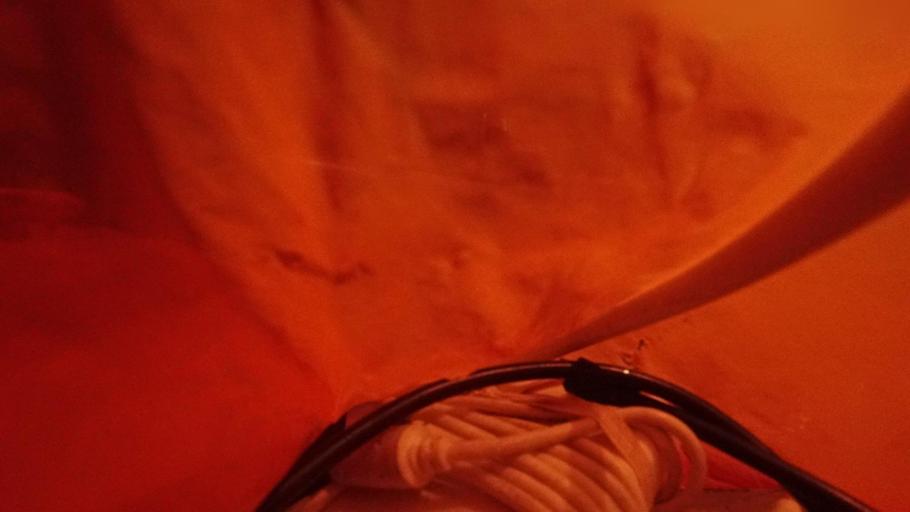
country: RU
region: Jewish Autonomous Oblast
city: Khingansk
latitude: 49.1629
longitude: 130.7728
